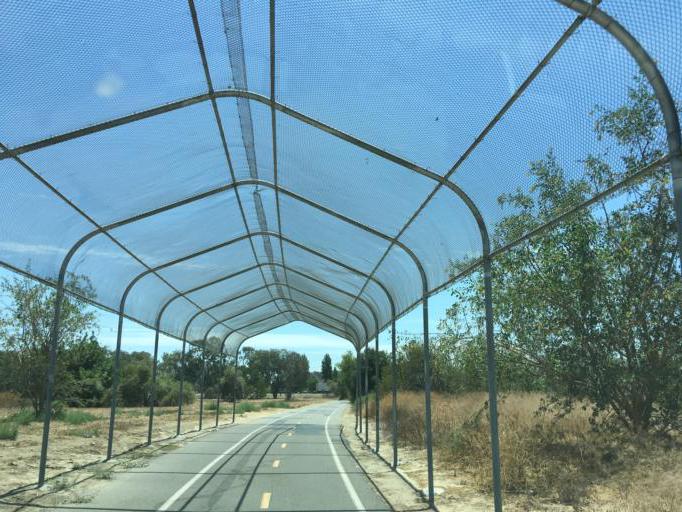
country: US
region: California
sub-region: Los Angeles County
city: South El Monte
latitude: 34.0435
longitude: -118.0715
